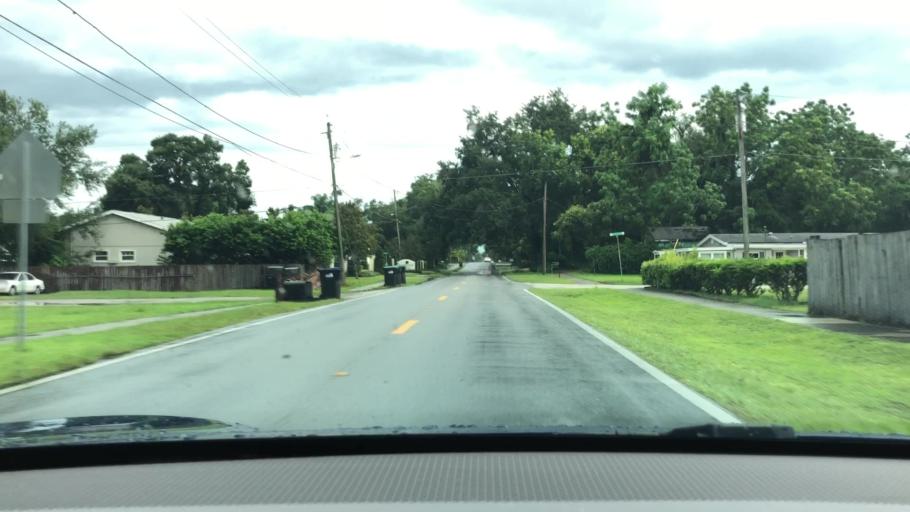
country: US
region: Florida
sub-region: Orange County
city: Conway
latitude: 28.5063
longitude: -81.3515
